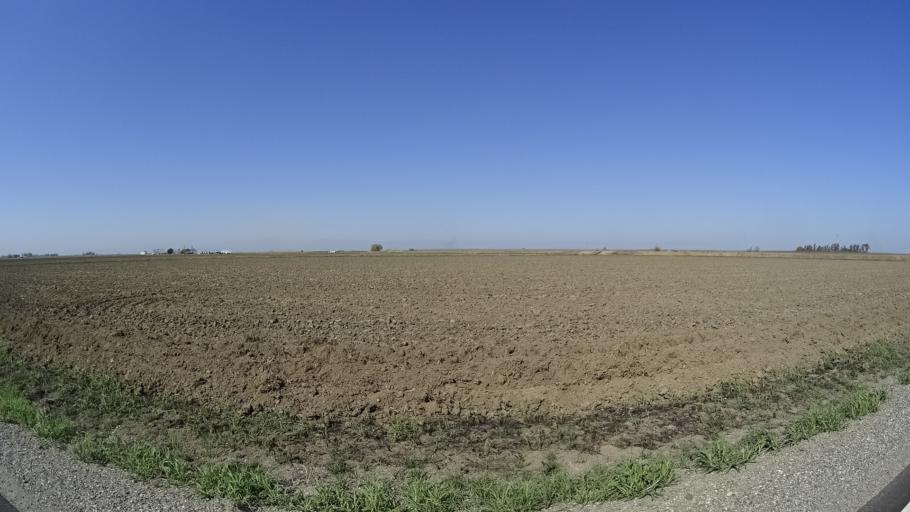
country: US
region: California
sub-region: Glenn County
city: Hamilton City
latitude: 39.6240
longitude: -122.0651
